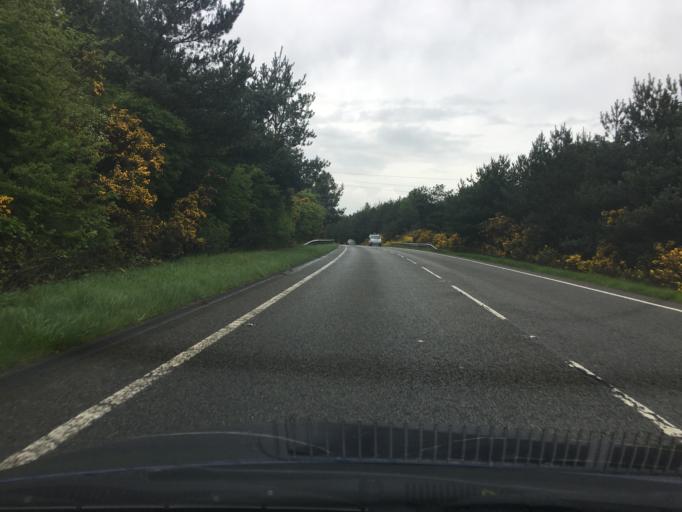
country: GB
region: England
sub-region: Bracknell Forest
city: Crowthorne
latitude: 51.3715
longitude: -0.7655
